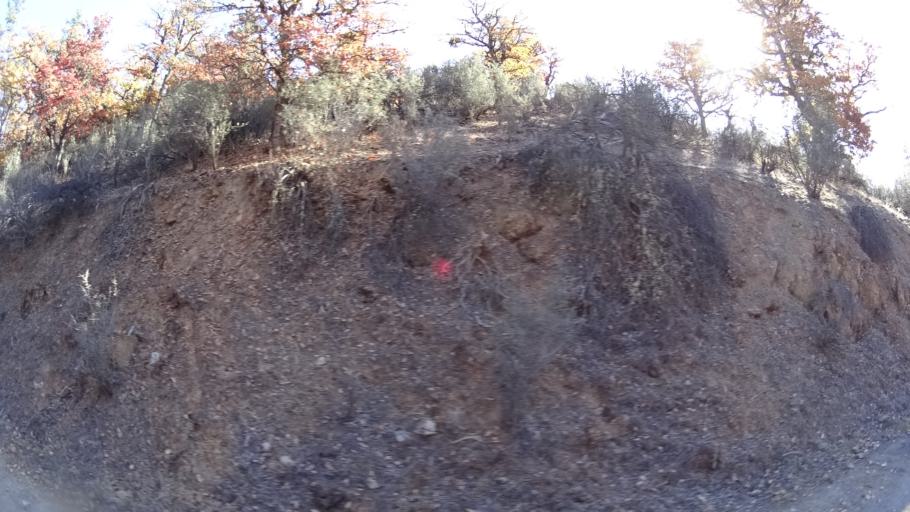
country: US
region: California
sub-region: Siskiyou County
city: Yreka
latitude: 41.8537
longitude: -122.8323
